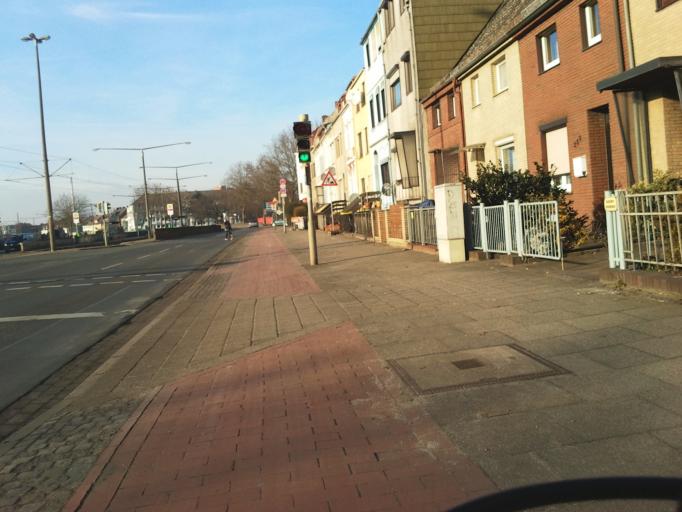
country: DE
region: Bremen
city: Bremen
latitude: 53.1081
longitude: 8.7646
